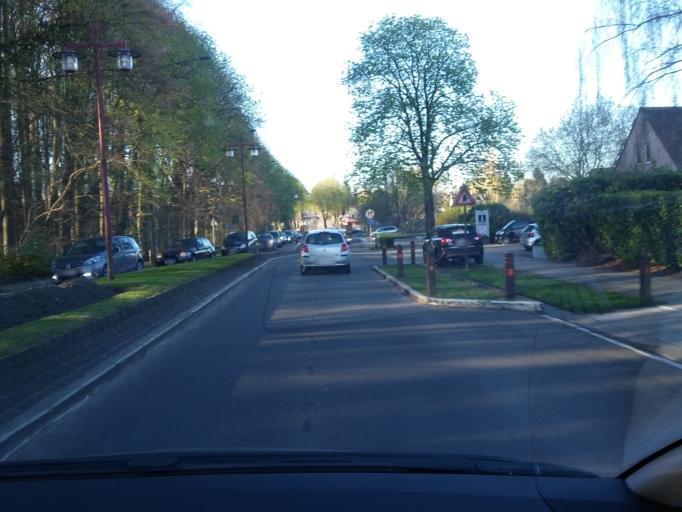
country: BE
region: Wallonia
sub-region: Province du Brabant Wallon
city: Waterloo
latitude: 50.7149
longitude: 4.4103
